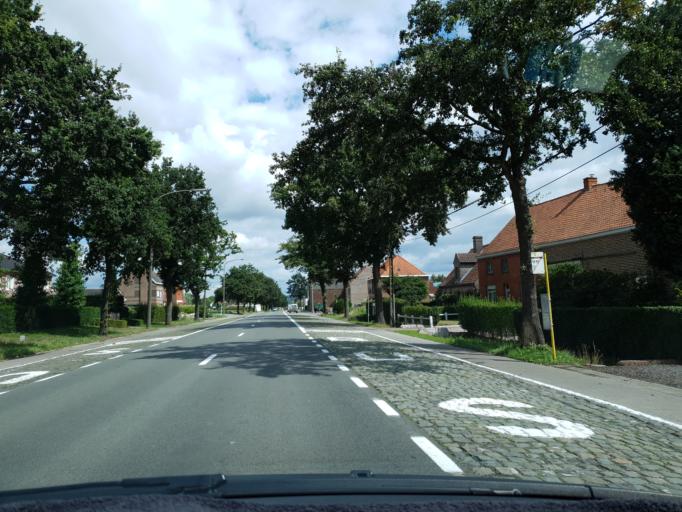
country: BE
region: Flanders
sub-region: Provincie Oost-Vlaanderen
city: Oudenaarde
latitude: 50.8118
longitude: 3.5592
